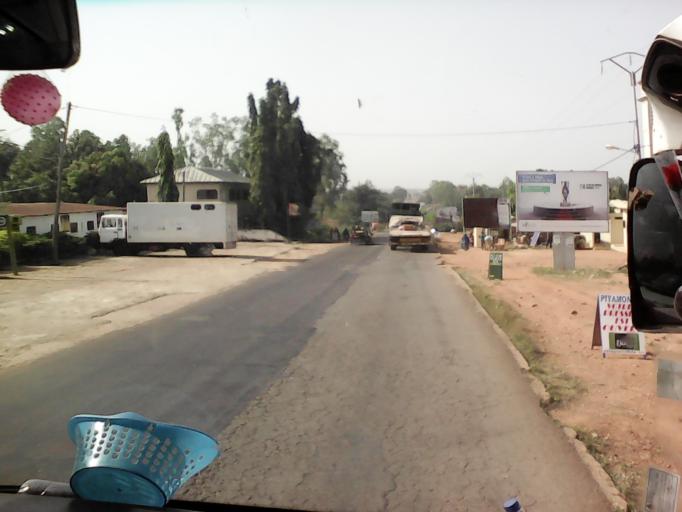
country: TG
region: Centrale
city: Sokode
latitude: 9.0164
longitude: 1.1391
